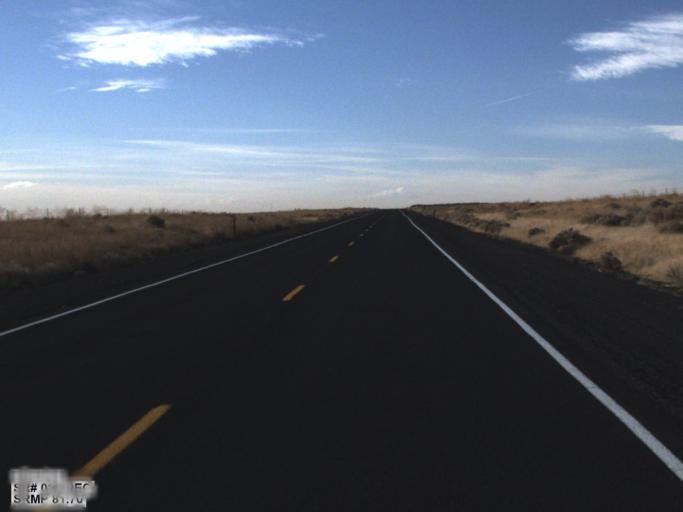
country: US
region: Washington
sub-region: Grant County
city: Warden
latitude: 47.3481
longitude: -118.9289
